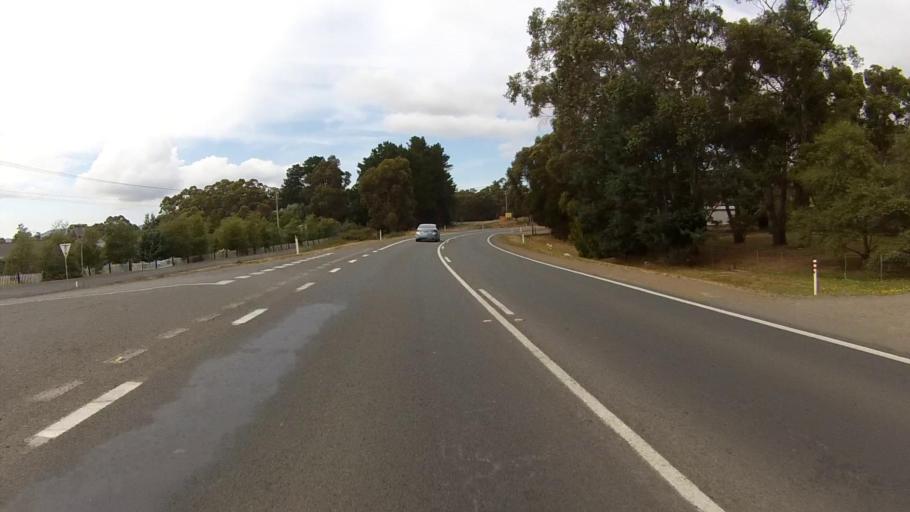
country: AU
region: Tasmania
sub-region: Kingborough
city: Margate
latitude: -43.0400
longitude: 147.2667
